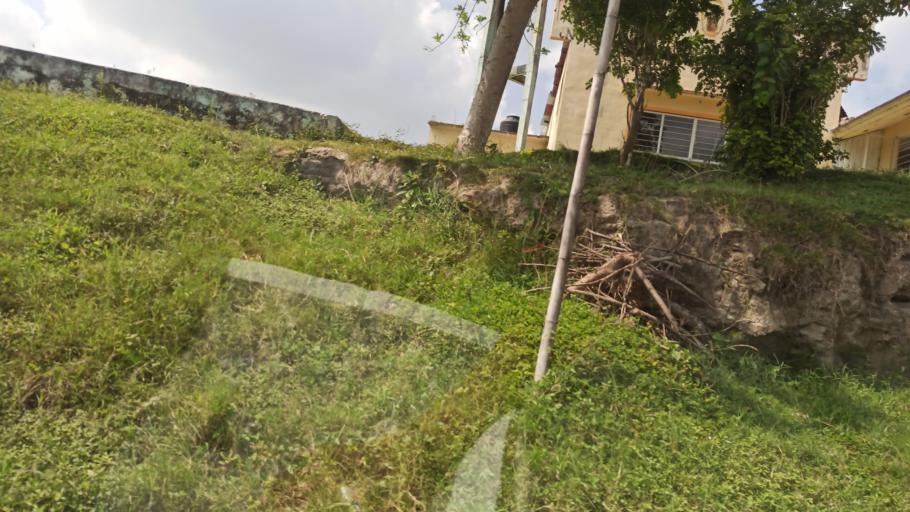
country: MX
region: Puebla
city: San Jose Acateno
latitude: 20.2277
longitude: -97.1217
